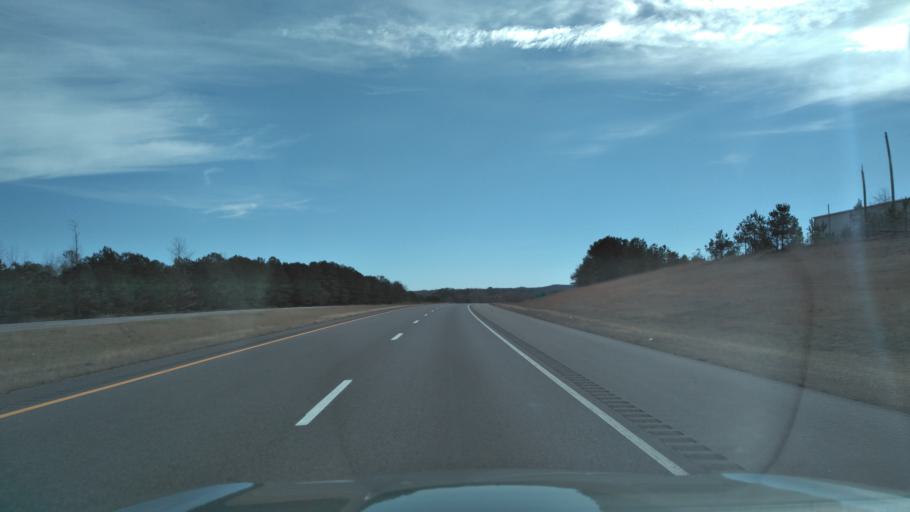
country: US
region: Alabama
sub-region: Marion County
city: Hamilton
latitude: 34.1738
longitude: -88.0689
